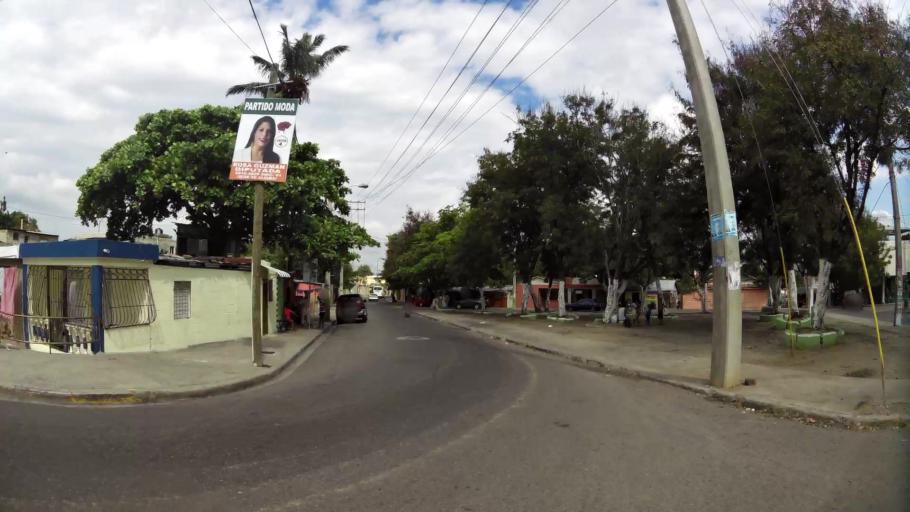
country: DO
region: Santiago
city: Santiago de los Caballeros
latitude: 19.4851
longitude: -70.7295
